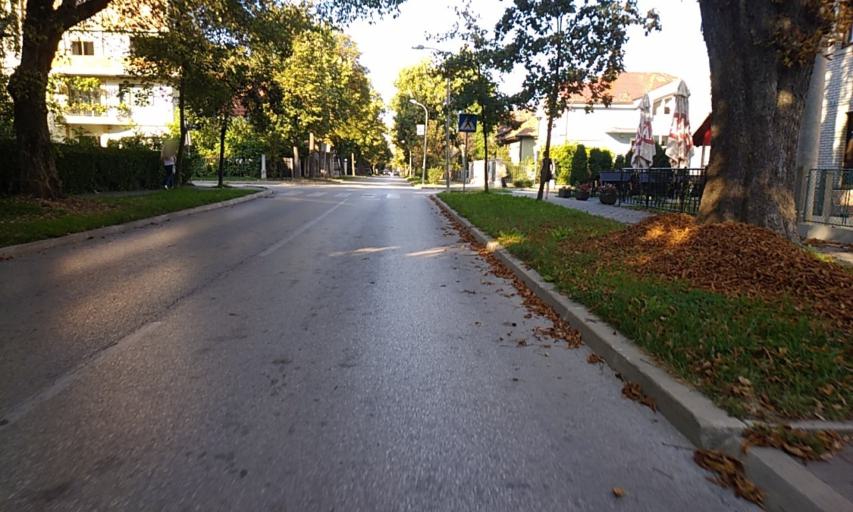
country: BA
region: Republika Srpska
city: Banja Luka
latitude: 44.7774
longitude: 17.1894
